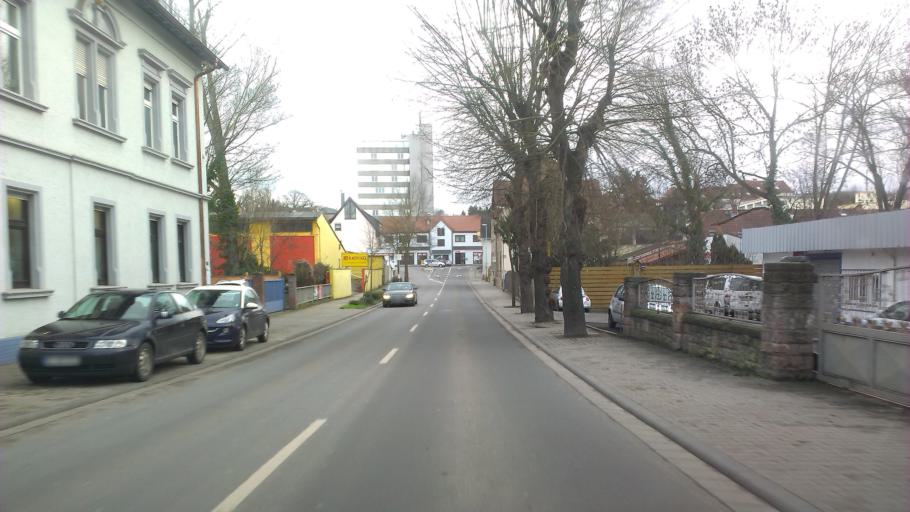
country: DE
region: Rheinland-Pfalz
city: Alzey
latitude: 49.7447
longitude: 8.1058
